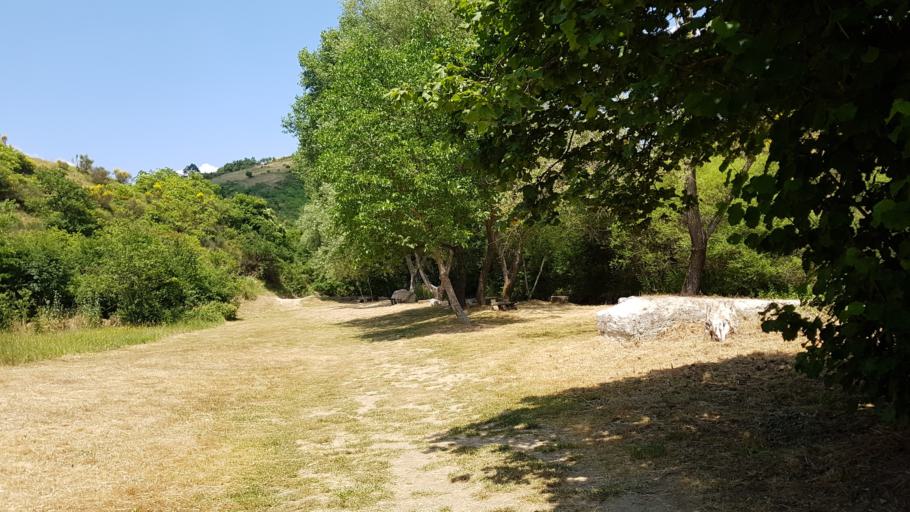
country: IT
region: Basilicate
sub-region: Provincia di Potenza
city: San Fele
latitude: 40.8137
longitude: 15.5279
